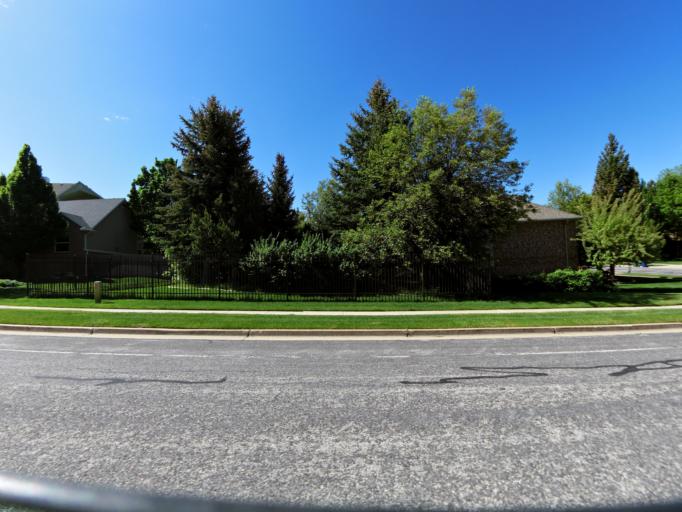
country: US
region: Utah
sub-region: Weber County
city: Uintah
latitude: 41.1669
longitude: -111.9302
